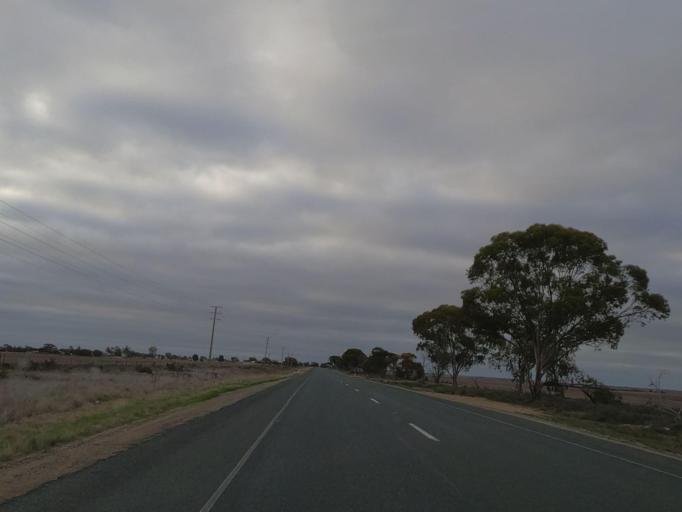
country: AU
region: Victoria
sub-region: Swan Hill
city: Swan Hill
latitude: -35.5897
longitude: 143.7904
